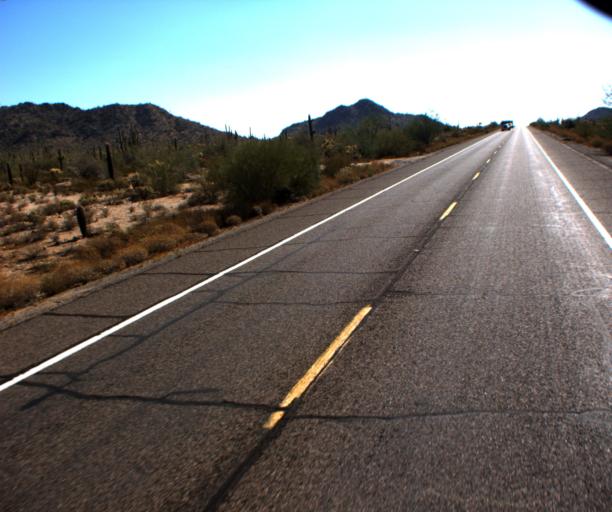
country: US
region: Arizona
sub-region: Pinal County
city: Sacaton
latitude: 33.0081
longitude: -111.6998
